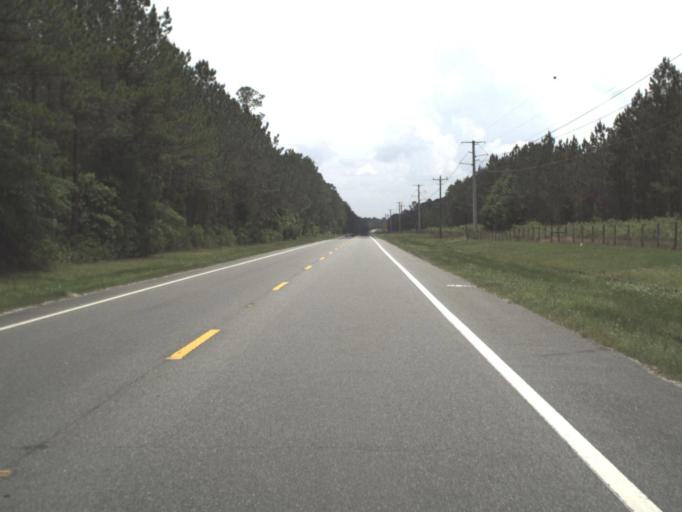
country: US
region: Florida
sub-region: Clay County
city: Asbury Lake
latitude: 29.9257
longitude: -81.8974
